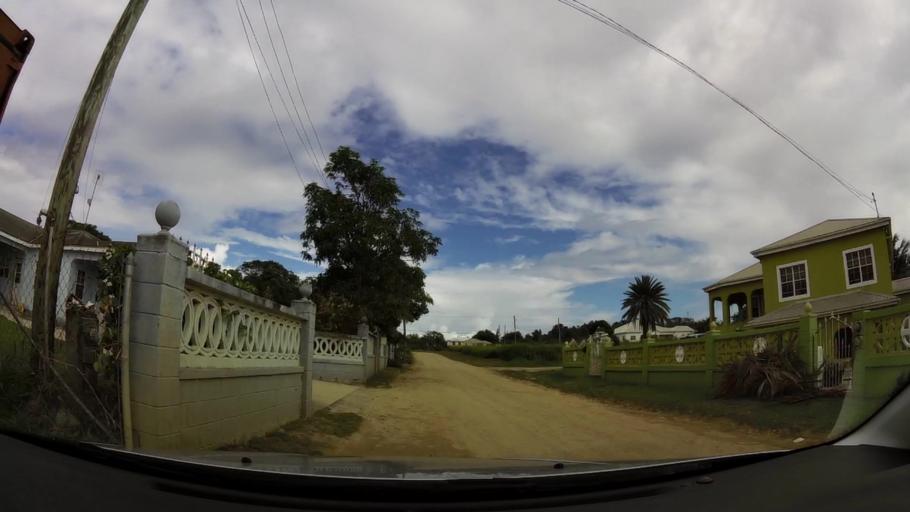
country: AG
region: Saint John
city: Potters Village
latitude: 17.0923
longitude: -61.8148
